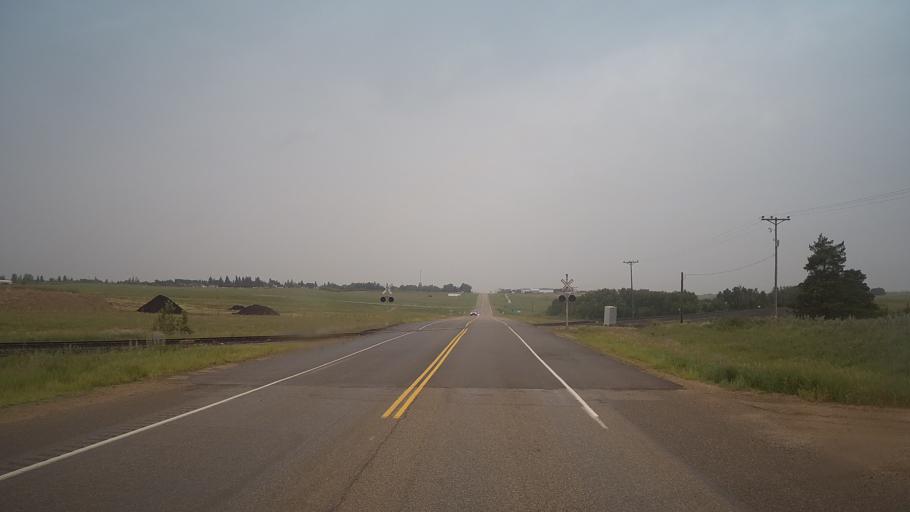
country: CA
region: Saskatchewan
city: Biggar
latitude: 52.0575
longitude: -107.9550
